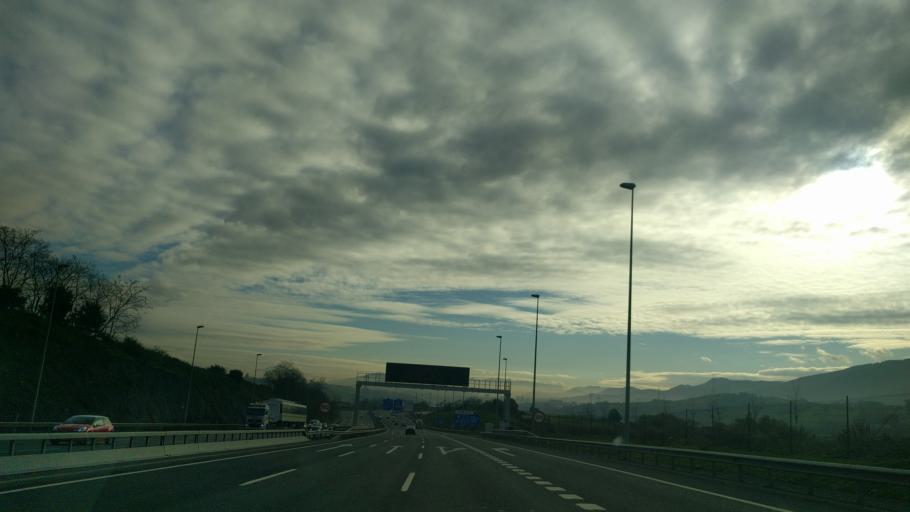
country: ES
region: Basque Country
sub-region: Bizkaia
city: Urtuella
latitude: 43.3251
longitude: -3.0627
